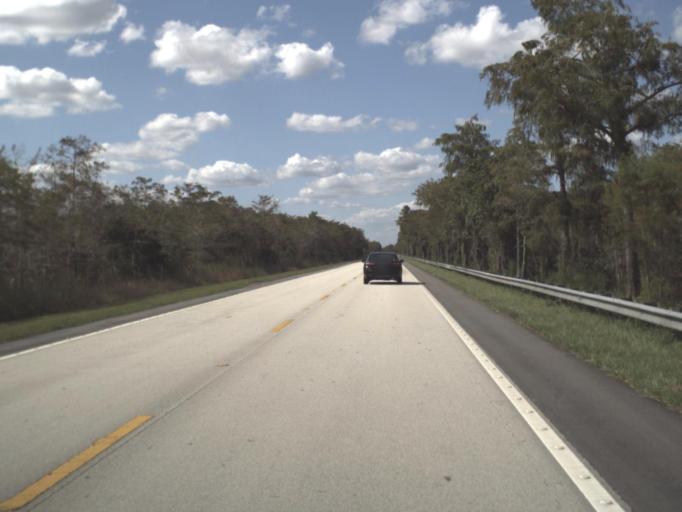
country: US
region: Florida
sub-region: Miami-Dade County
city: Kendall West
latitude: 25.8372
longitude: -80.9101
